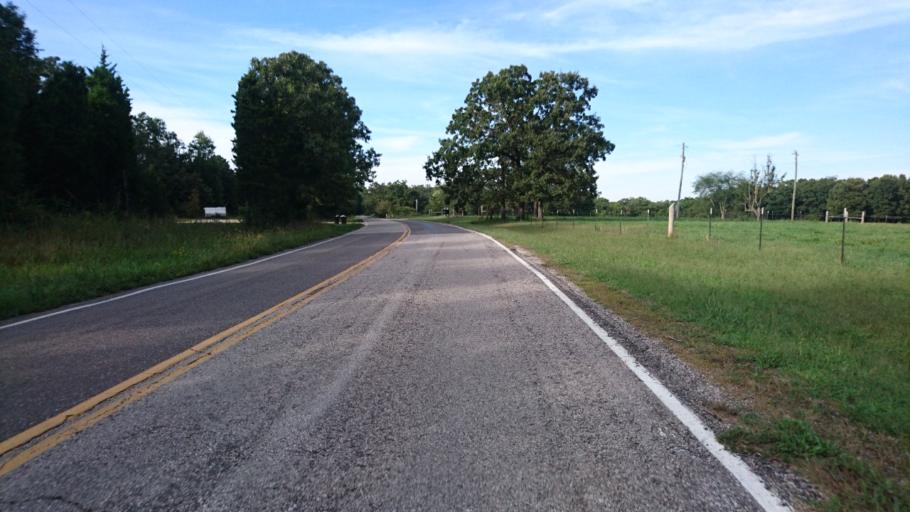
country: US
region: Missouri
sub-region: Crawford County
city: Cuba
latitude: 38.1007
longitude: -91.3629
